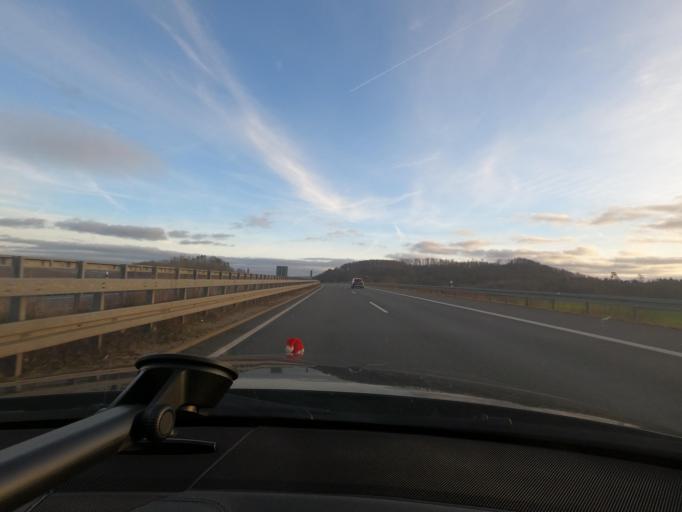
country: DE
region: Lower Saxony
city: Gemeinde Friedland
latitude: 51.4066
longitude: 9.9117
